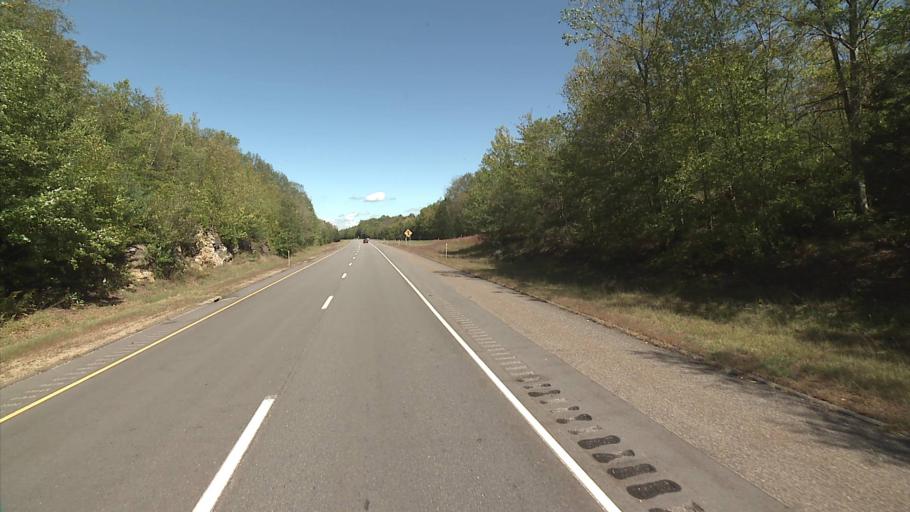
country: US
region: Connecticut
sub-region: New London County
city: Colchester
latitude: 41.5041
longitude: -72.3013
